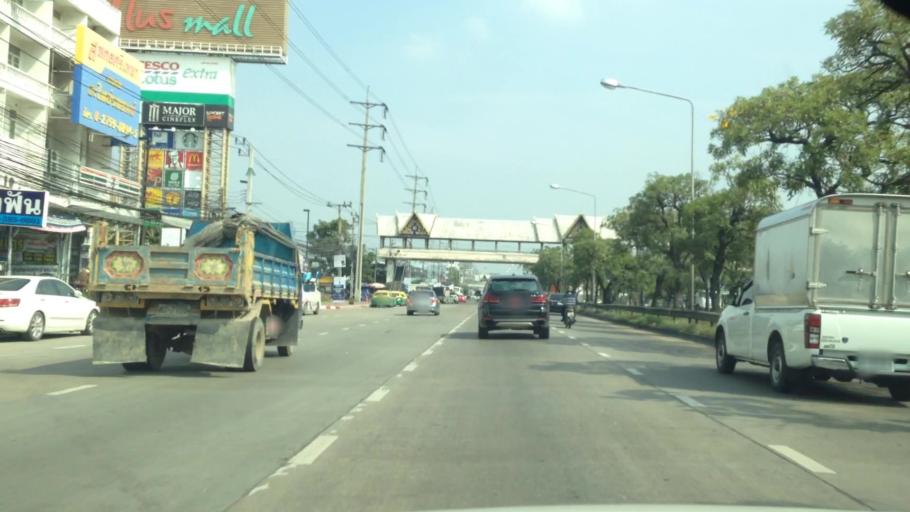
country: TH
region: Samut Prakan
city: Samut Prakan
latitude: 13.6192
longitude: 100.6224
